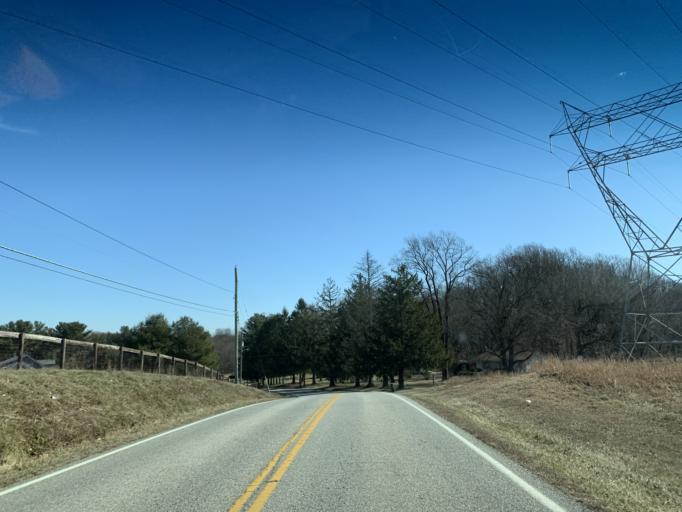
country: US
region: Maryland
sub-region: Cecil County
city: Rising Sun
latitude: 39.6329
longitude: -76.0900
